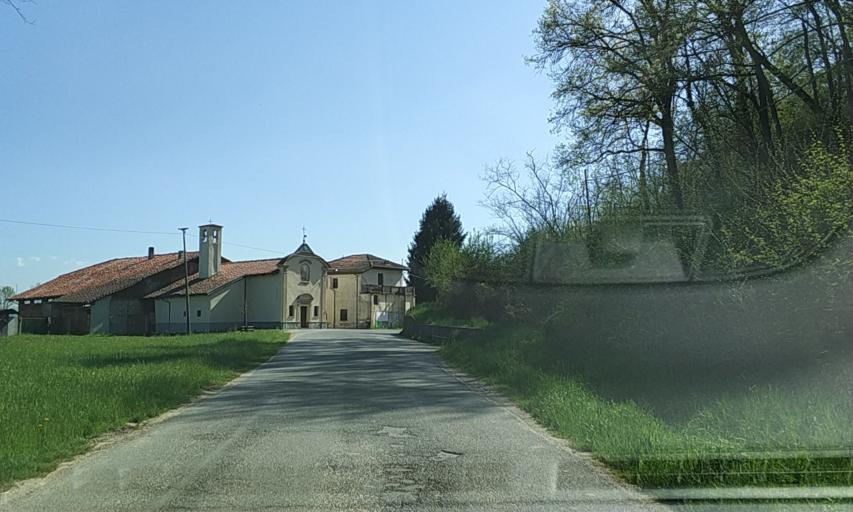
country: IT
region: Piedmont
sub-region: Provincia di Torino
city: Rivara
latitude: 45.3191
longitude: 7.6427
